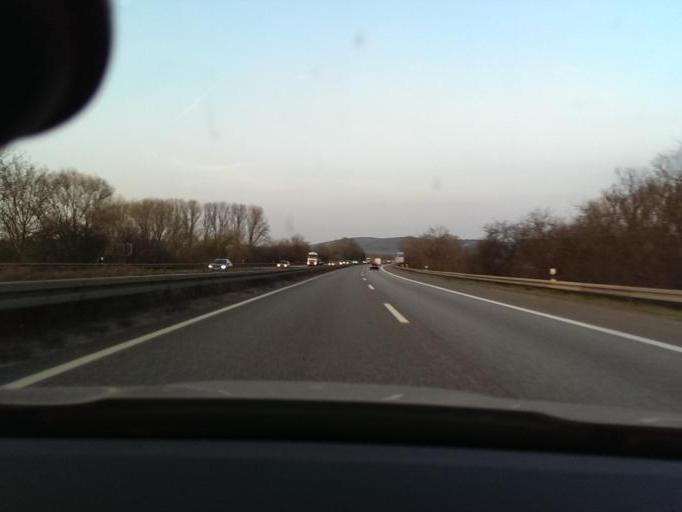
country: DE
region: Lower Saxony
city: Hillerse
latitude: 51.7237
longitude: 9.9498
